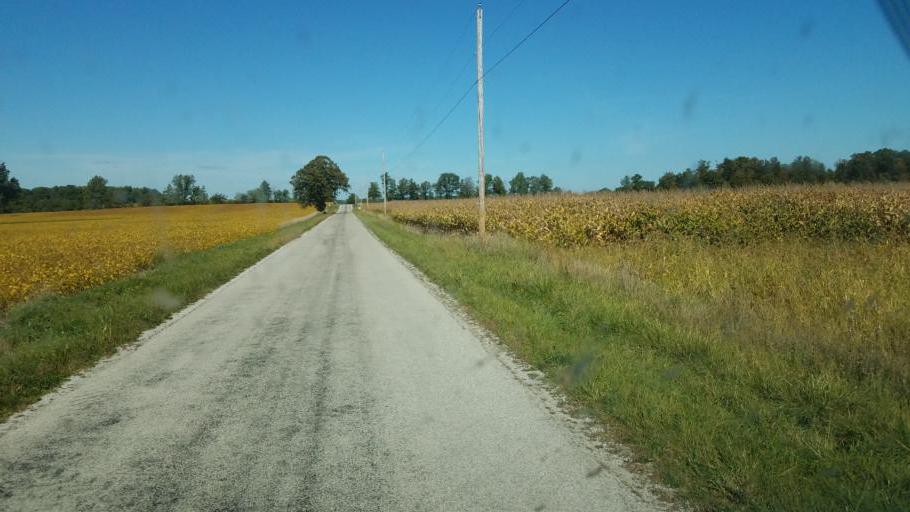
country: US
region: Ohio
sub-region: Huron County
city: Willard
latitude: 40.9495
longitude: -82.7972
